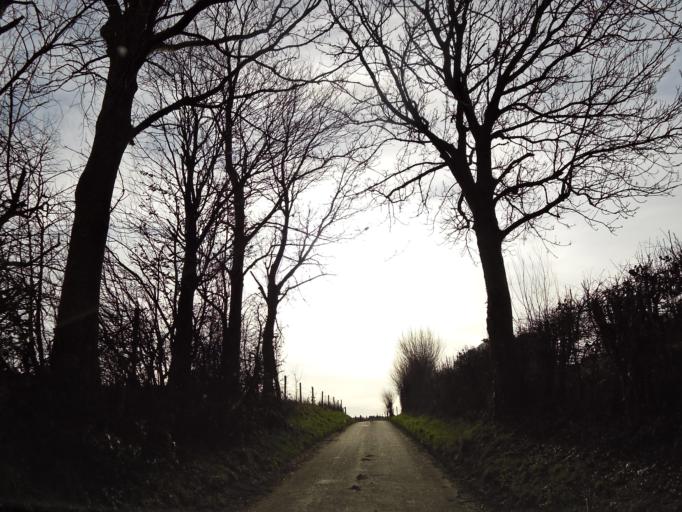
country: NL
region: Limburg
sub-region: Gemeente Voerendaal
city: Ubachsberg
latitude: 50.8389
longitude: 5.9214
